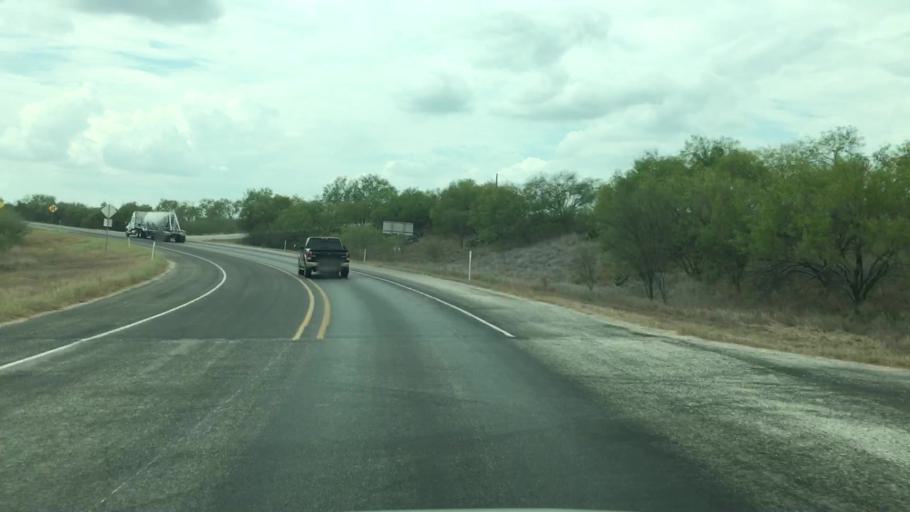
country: US
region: Texas
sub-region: Atascosa County
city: Pleasanton
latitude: 28.7841
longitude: -98.3156
